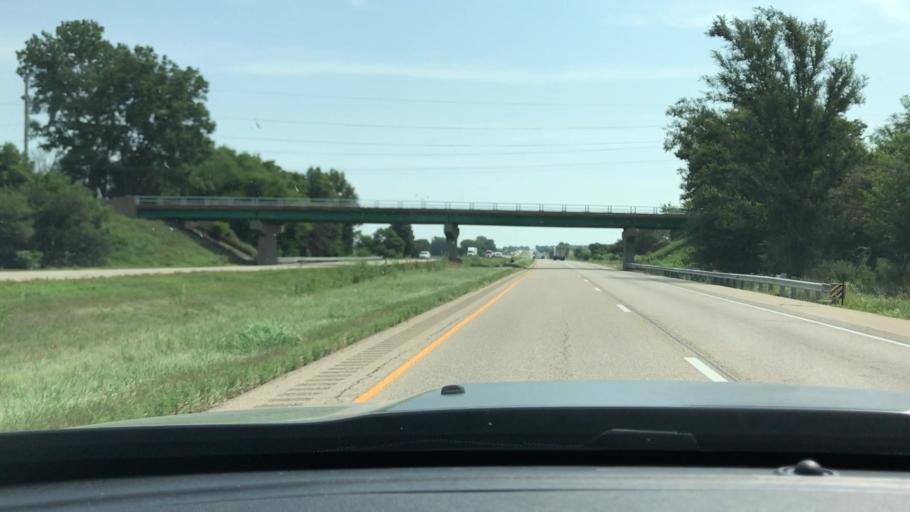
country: US
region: Illinois
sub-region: Henry County
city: Kewanee
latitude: 41.3864
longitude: -89.7673
